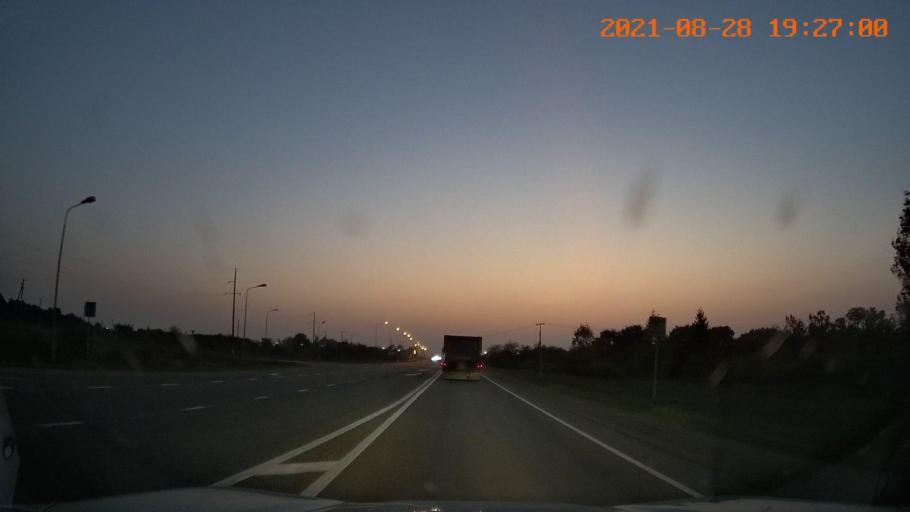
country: RU
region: Adygeya
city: Ponezhukay
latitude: 44.8786
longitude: 39.3872
